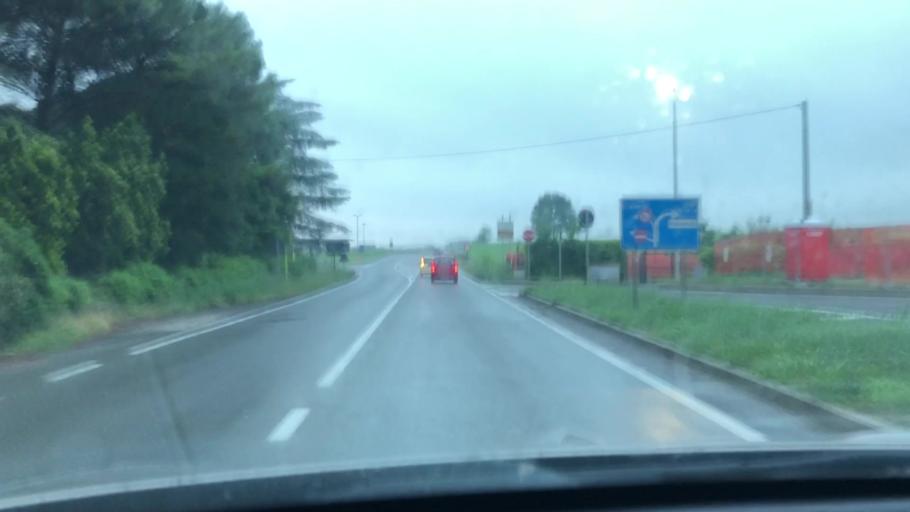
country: IT
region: Tuscany
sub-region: Province of Pisa
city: Val di Cava
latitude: 43.6415
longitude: 10.6502
